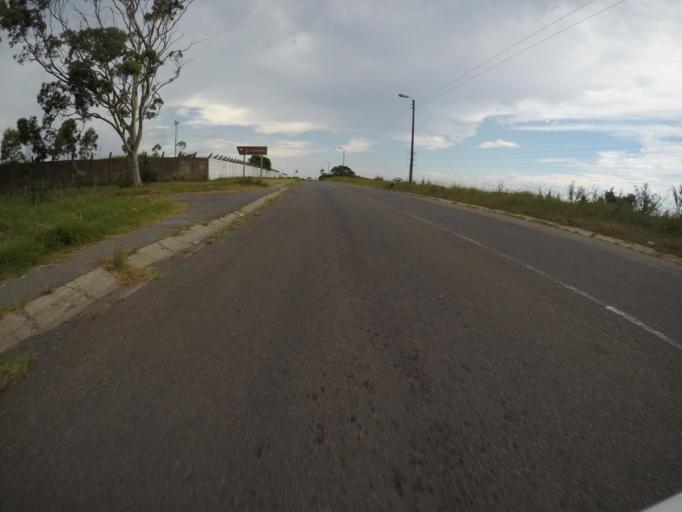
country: ZA
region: Eastern Cape
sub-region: Buffalo City Metropolitan Municipality
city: East London
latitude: -33.0254
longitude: 27.8625
